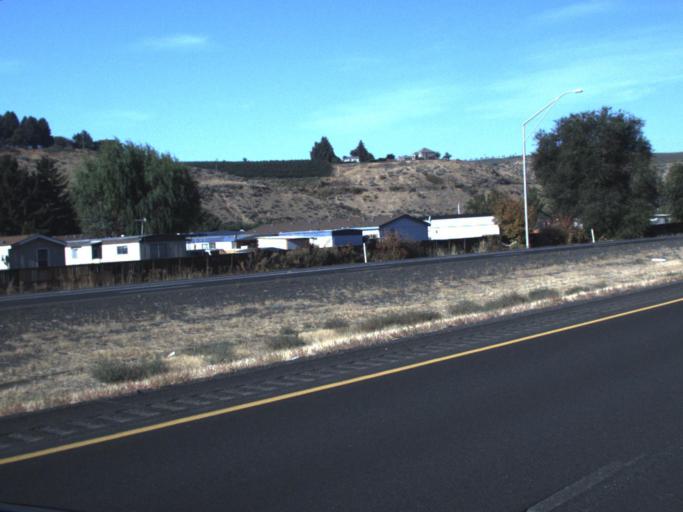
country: US
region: Washington
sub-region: Yakima County
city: West Valley
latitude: 46.6242
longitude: -120.5702
